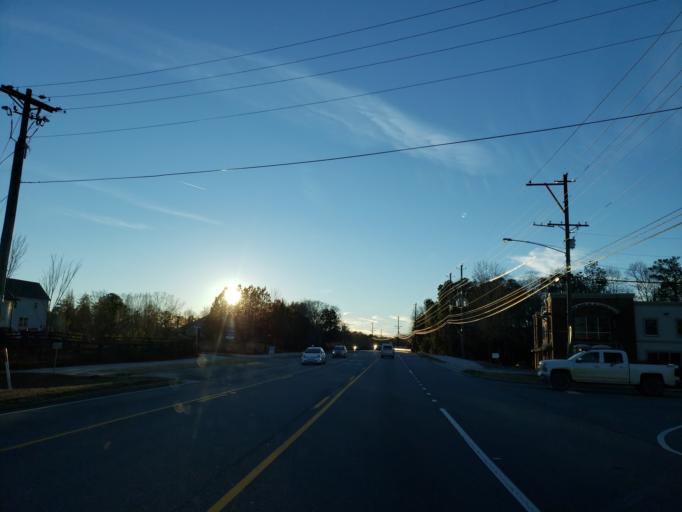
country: US
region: Georgia
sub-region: Fulton County
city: Alpharetta
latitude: 34.0917
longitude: -84.2899
